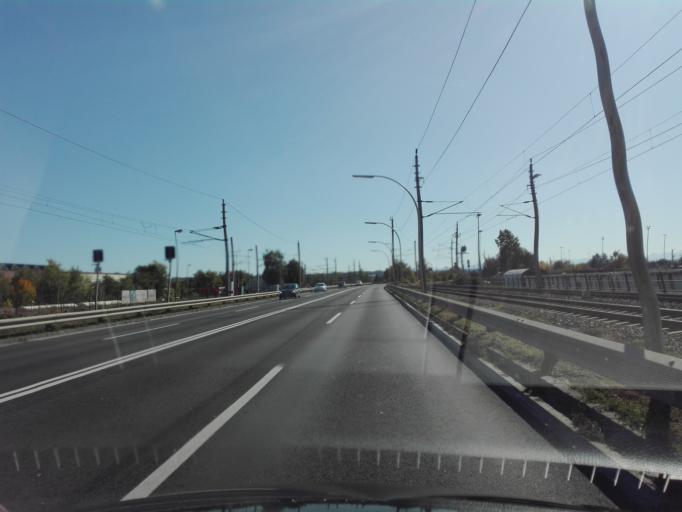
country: AT
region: Upper Austria
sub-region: Linz Stadt
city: Linz
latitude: 48.2683
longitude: 14.3210
